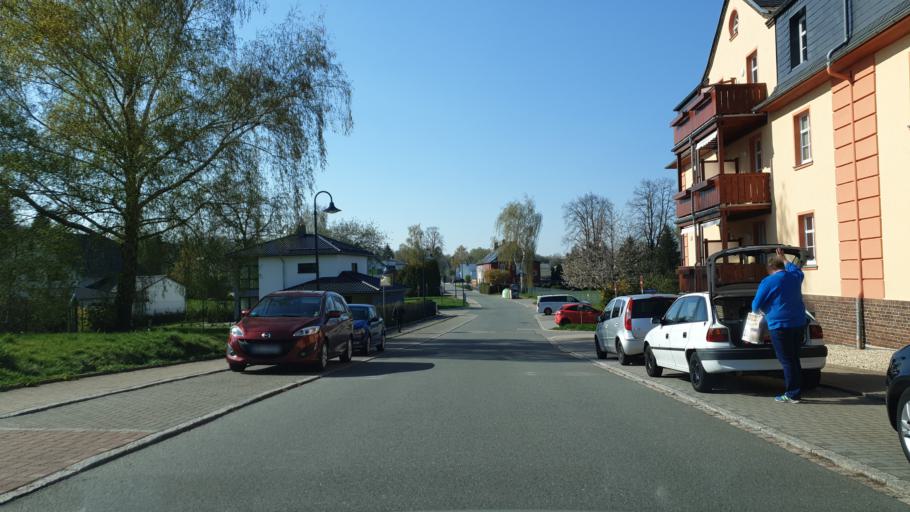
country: DE
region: Saxony
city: Oelsnitz
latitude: 50.7280
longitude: 12.7054
